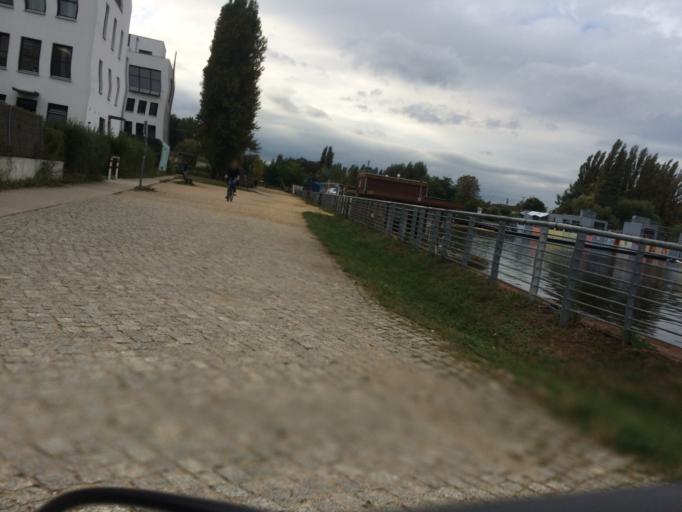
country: DE
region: Berlin
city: Treptow Bezirk
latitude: 52.4979
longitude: 13.4713
